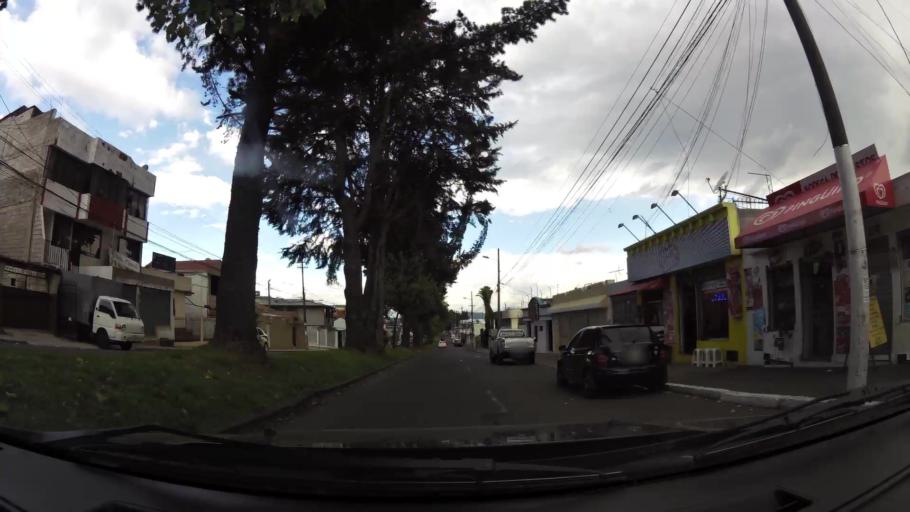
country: EC
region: Pichincha
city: Quito
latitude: -0.1363
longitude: -78.4865
